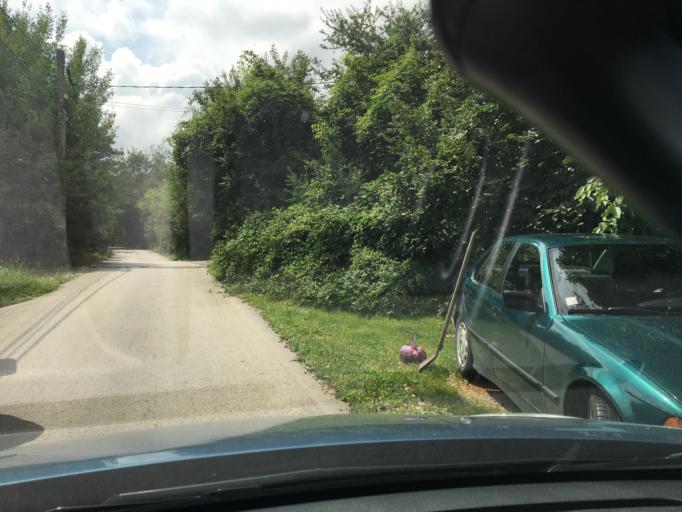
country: BG
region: Sofia-Capital
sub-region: Stolichna Obshtina
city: Sofia
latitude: 42.6070
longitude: 23.3659
